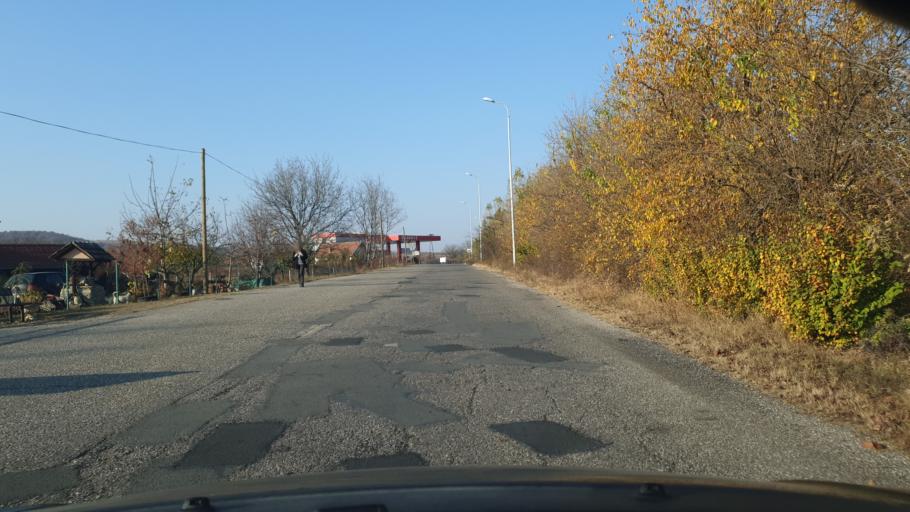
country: RS
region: Central Serbia
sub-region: Borski Okrug
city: Negotin
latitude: 44.2396
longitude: 22.5171
